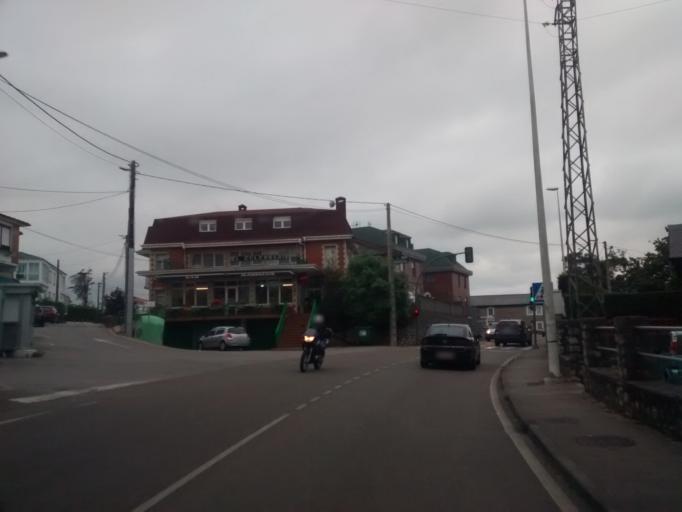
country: ES
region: Cantabria
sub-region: Provincia de Cantabria
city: Santander
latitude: 43.4440
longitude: -3.7681
